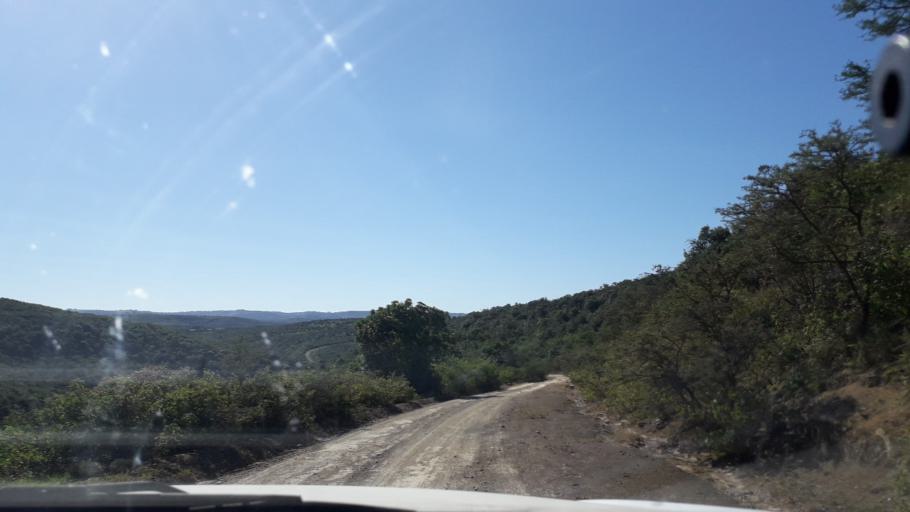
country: ZA
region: Eastern Cape
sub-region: Amathole District Municipality
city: Komga
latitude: -32.7748
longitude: 27.9596
